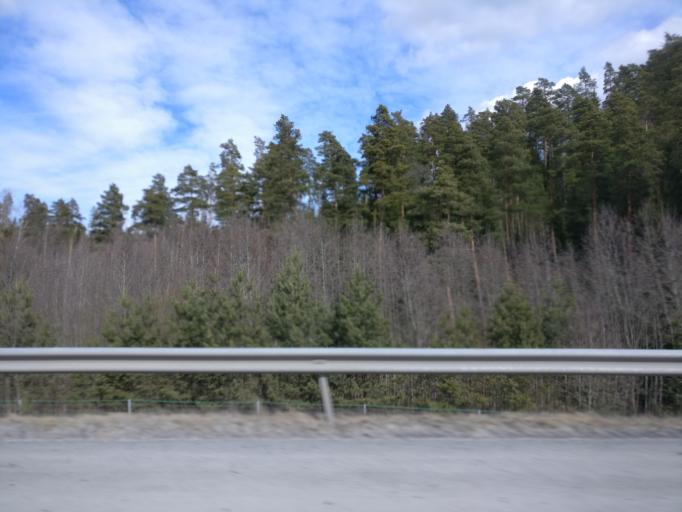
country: FI
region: Haeme
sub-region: Haemeenlinna
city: Parola
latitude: 61.0625
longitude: 24.3298
